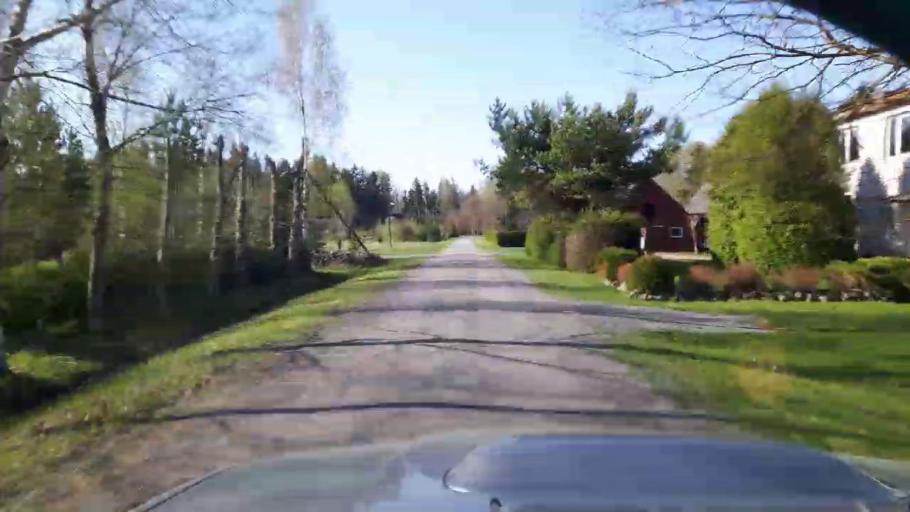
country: EE
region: Paernumaa
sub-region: Tootsi vald
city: Tootsi
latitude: 58.4867
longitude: 24.9065
